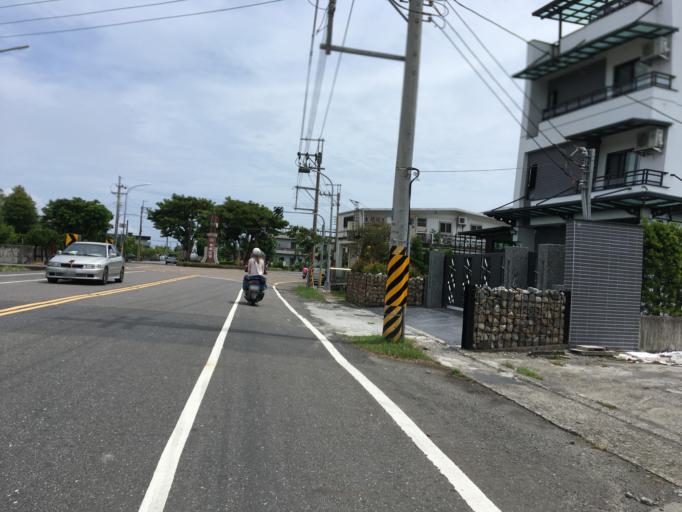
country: TW
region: Taiwan
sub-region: Yilan
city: Yilan
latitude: 24.6930
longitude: 121.8077
